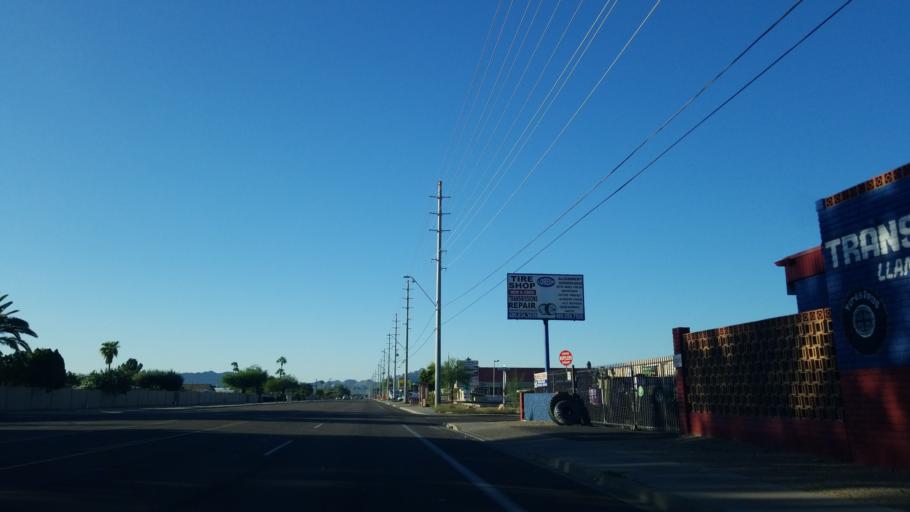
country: US
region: Arizona
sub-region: Maricopa County
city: Paradise Valley
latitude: 33.6375
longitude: -112.0136
